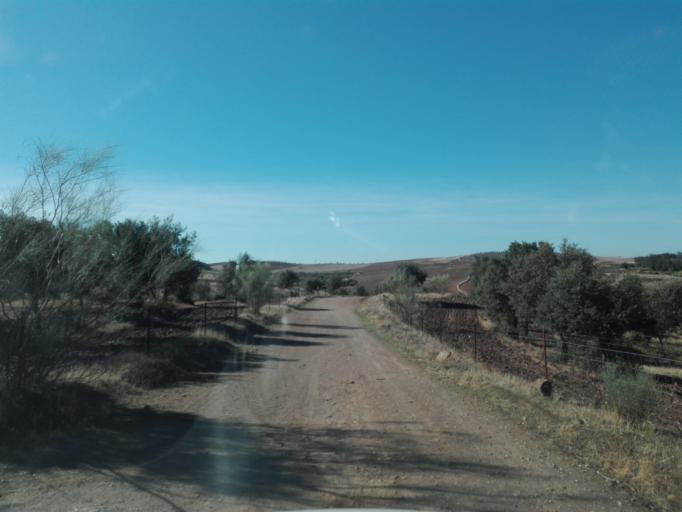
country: ES
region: Extremadura
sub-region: Provincia de Badajoz
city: Llera
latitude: 38.4460
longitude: -6.0430
